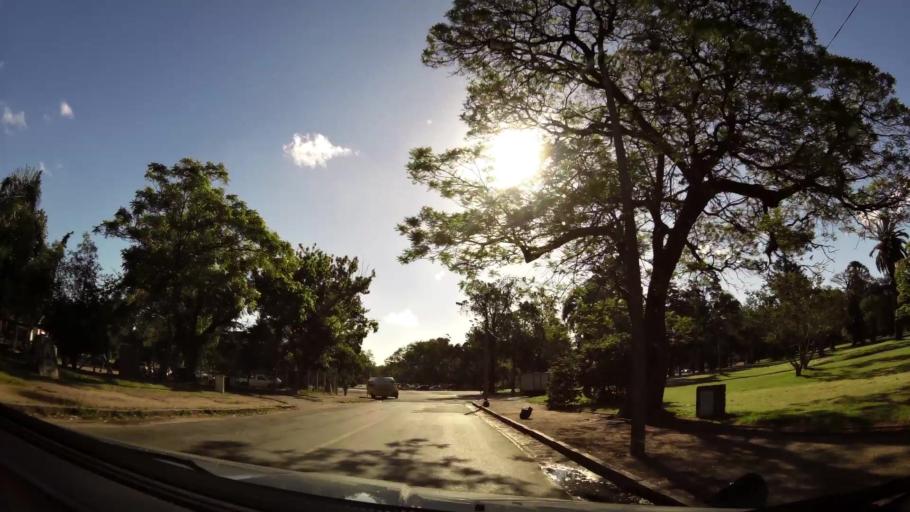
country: UY
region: Montevideo
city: Montevideo
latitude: -34.8570
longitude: -56.2041
